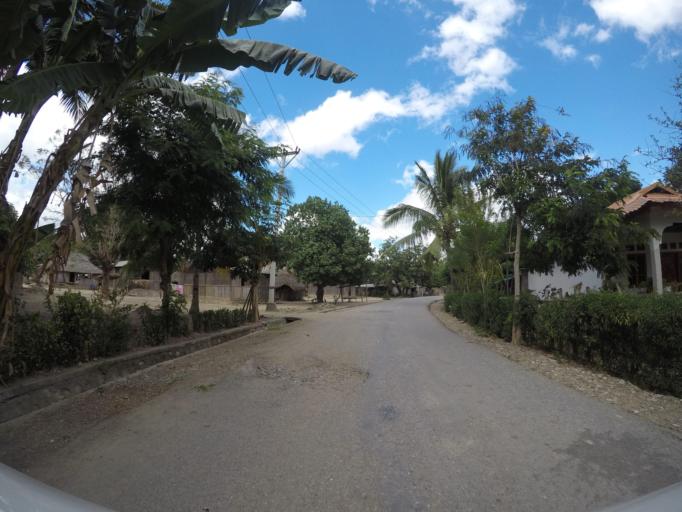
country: TL
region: Lautem
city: Lospalos
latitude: -8.4521
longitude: 126.8228
